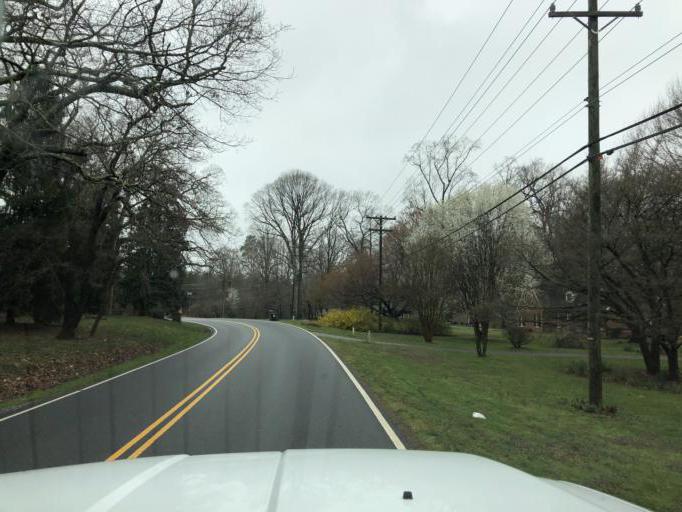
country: US
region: North Carolina
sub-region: Mecklenburg County
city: Huntersville
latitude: 35.3467
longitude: -80.8953
